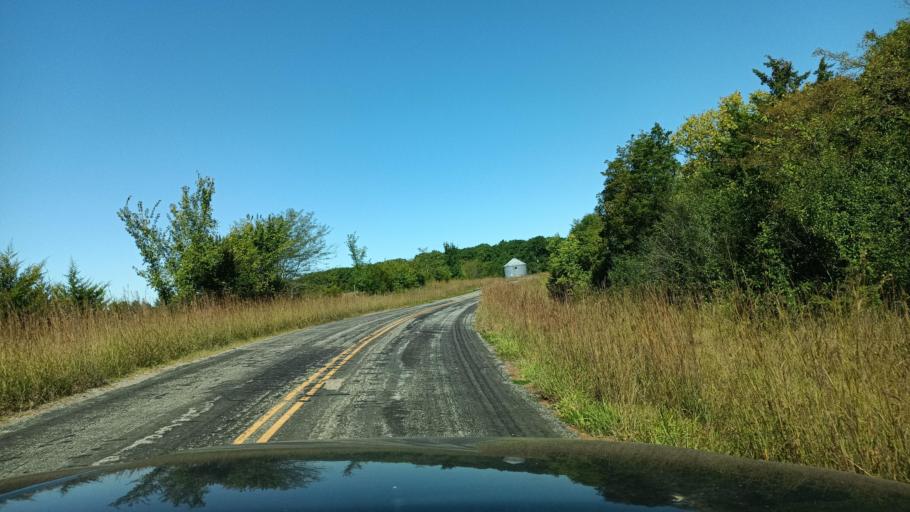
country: US
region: Missouri
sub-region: Scotland County
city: Memphis
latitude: 40.3540
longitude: -92.3539
